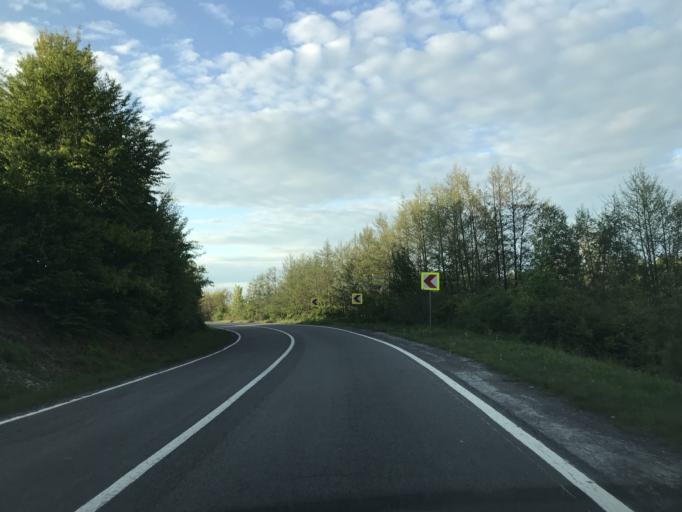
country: RO
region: Sibiu
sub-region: Comuna Cartisoara
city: Cartisoara
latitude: 45.7011
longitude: 24.5708
